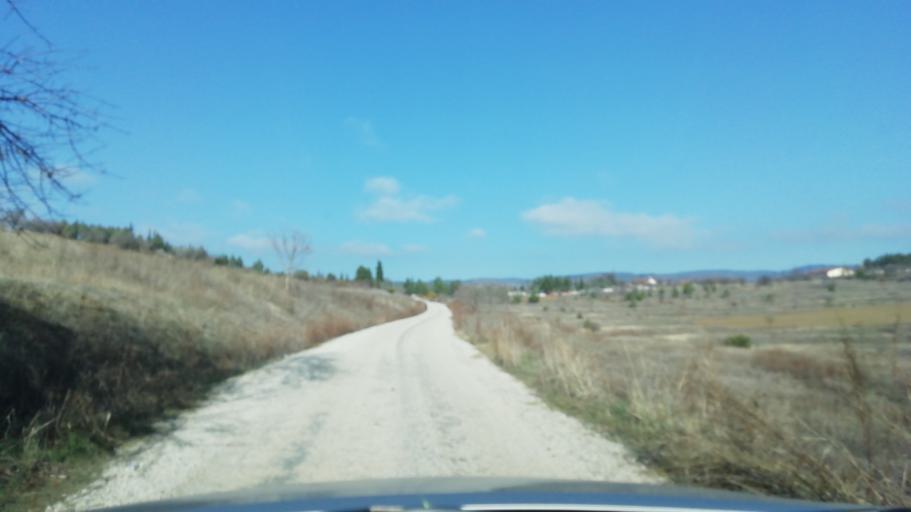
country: TR
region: Karabuk
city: Safranbolu
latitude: 41.2271
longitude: 32.7761
